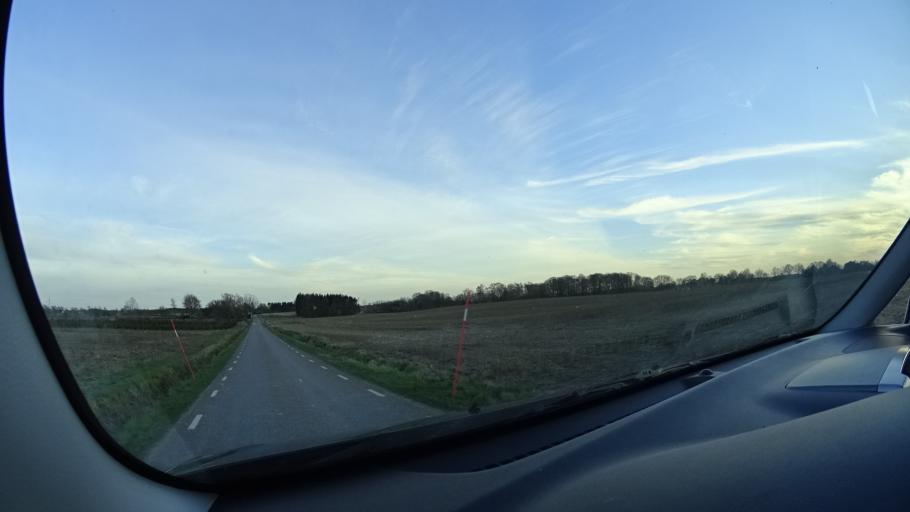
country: SE
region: Skane
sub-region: Eslovs Kommun
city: Stehag
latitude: 55.8711
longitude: 13.4445
